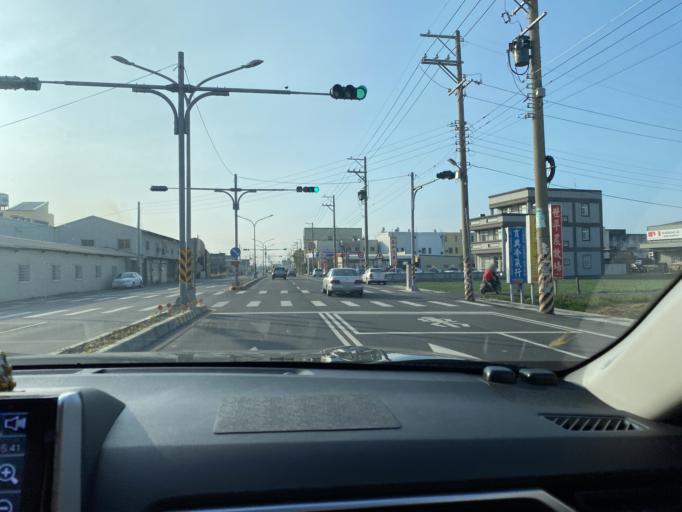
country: TW
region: Taiwan
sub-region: Changhua
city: Chang-hua
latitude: 23.9529
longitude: 120.4369
